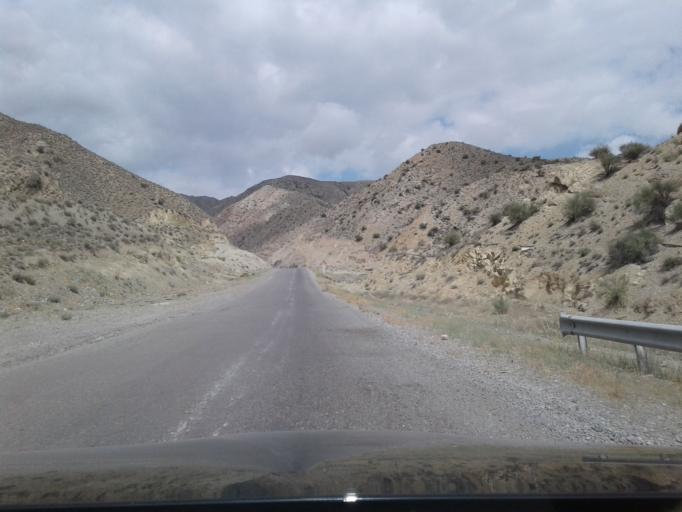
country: TM
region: Ahal
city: Baharly
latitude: 38.5057
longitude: 57.0617
